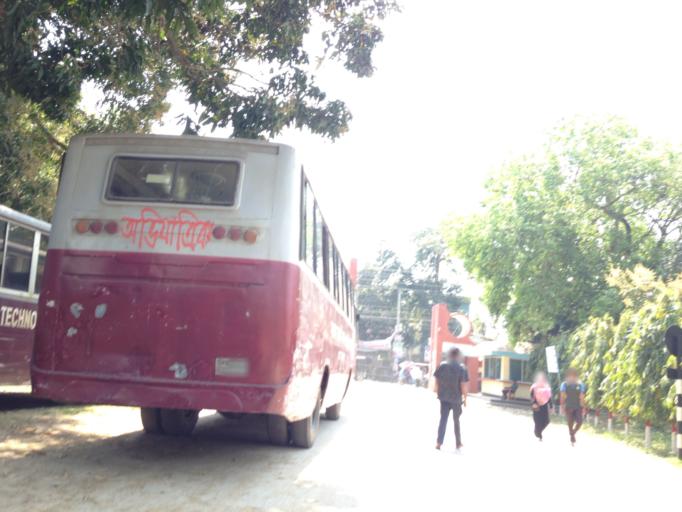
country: BD
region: Dhaka
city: Tangail
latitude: 24.2342
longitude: 89.8924
